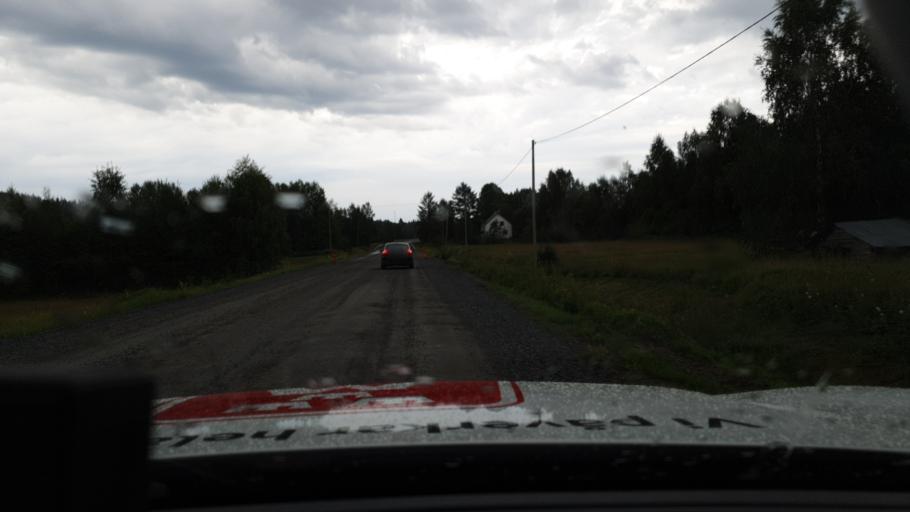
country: SE
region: Norrbotten
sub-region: Bodens Kommun
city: Boden
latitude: 65.8526
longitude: 21.4992
